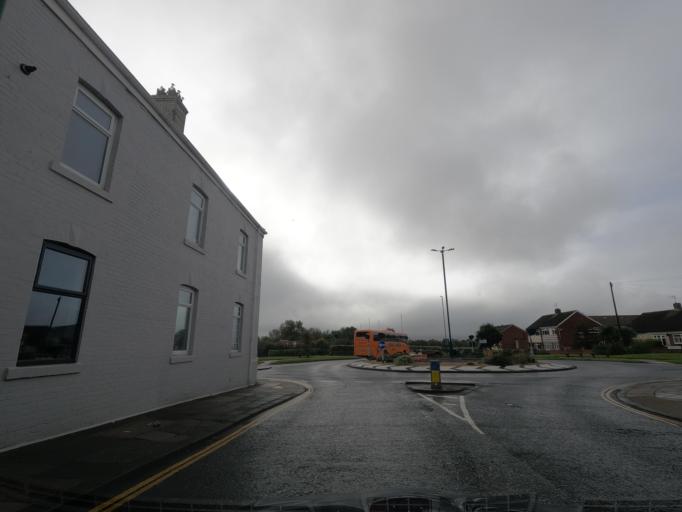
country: GB
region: England
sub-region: Redcar and Cleveland
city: Redcar
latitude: 54.6170
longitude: -1.0851
